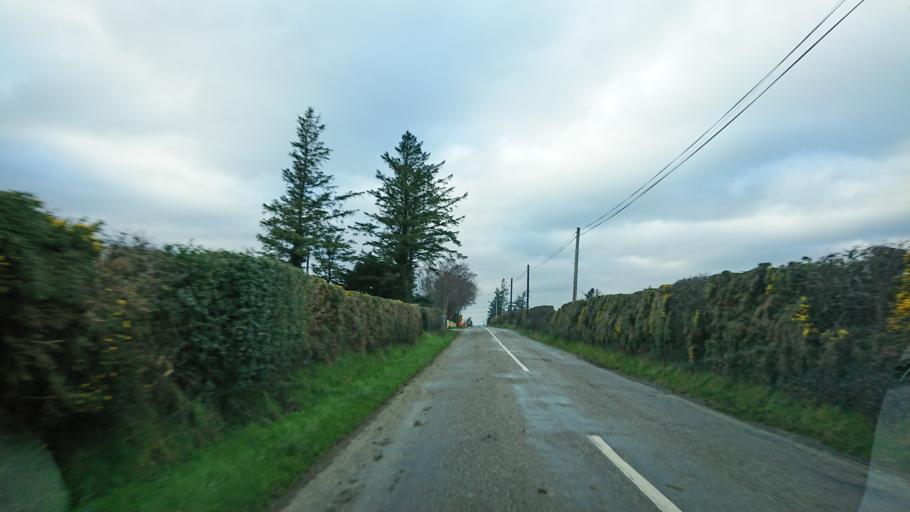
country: IE
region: Munster
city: Carrick-on-Suir
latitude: 52.3124
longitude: -7.5243
